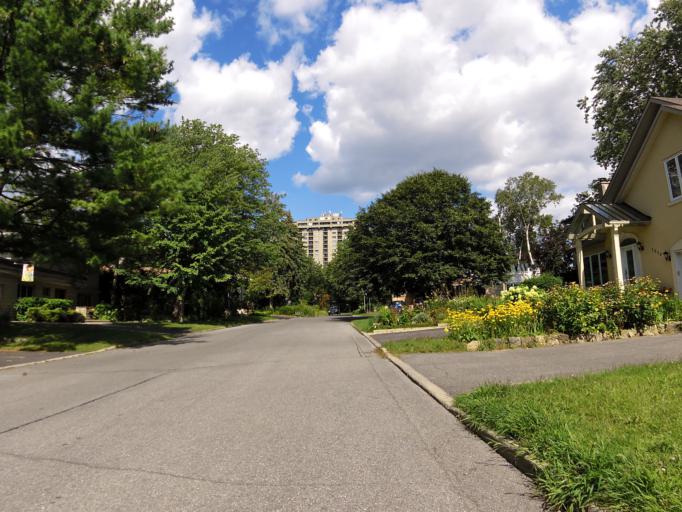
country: CA
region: Ontario
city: Ottawa
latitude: 45.3678
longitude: -75.7485
